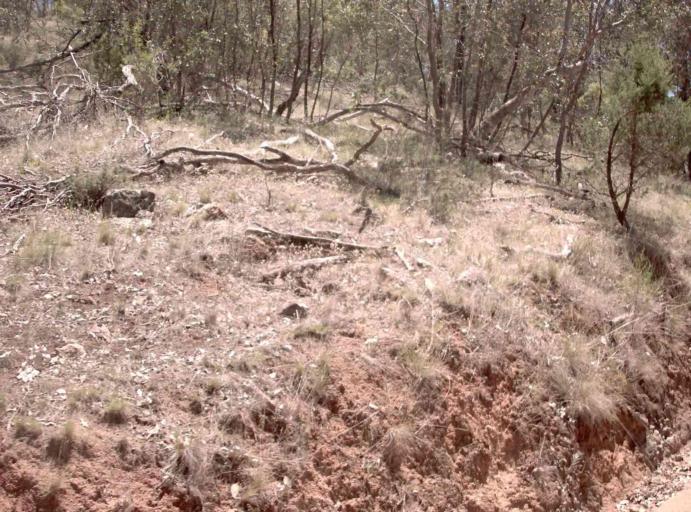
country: AU
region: New South Wales
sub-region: Snowy River
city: Jindabyne
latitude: -36.9017
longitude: 148.4171
